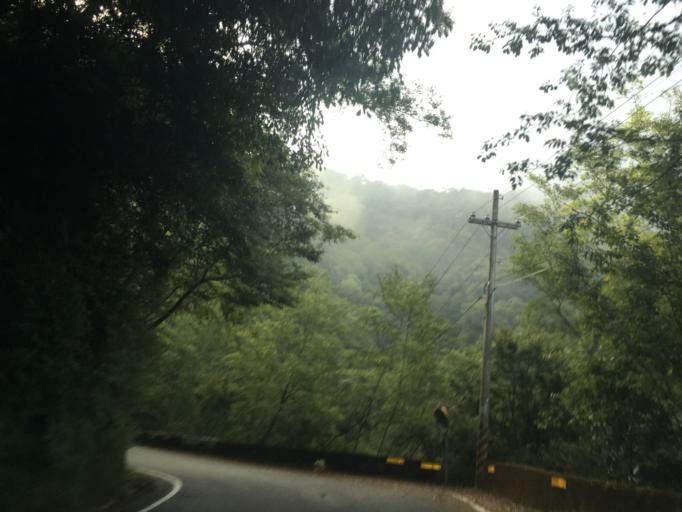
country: TW
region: Taiwan
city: Fengyuan
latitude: 24.2363
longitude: 120.9777
